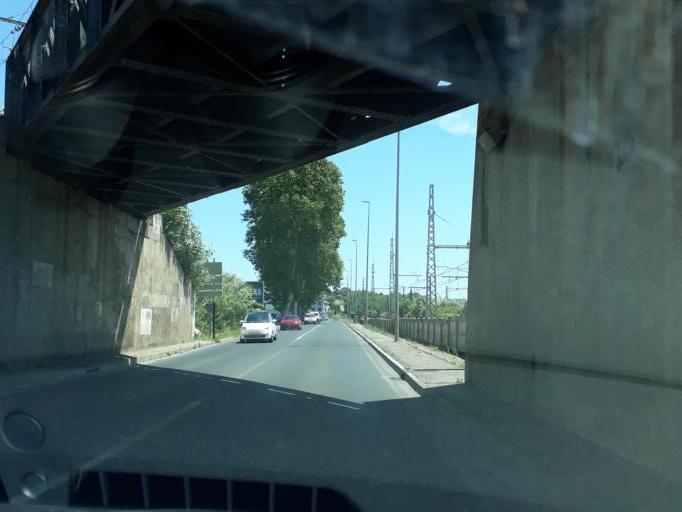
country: FR
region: Languedoc-Roussillon
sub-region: Departement de l'Herault
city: Beziers
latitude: 43.3327
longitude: 3.2339
